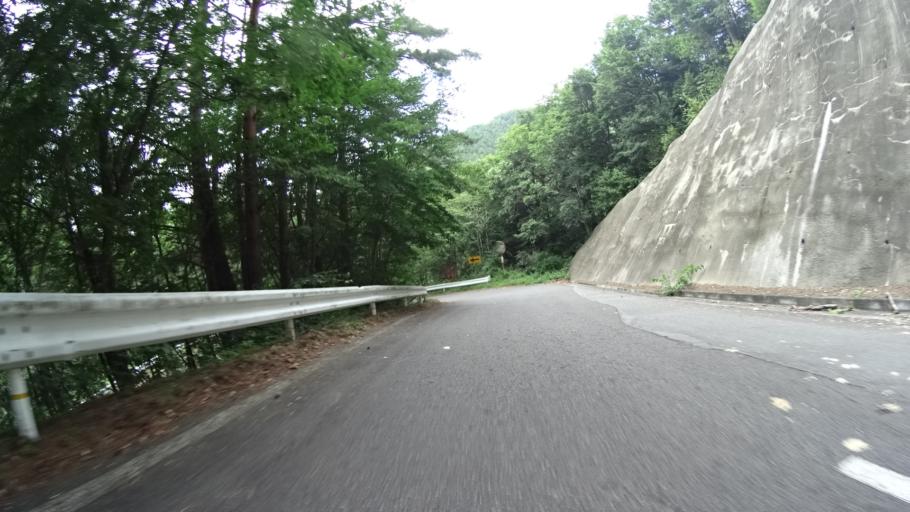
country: JP
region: Nagano
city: Saku
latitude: 36.0699
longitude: 138.6248
